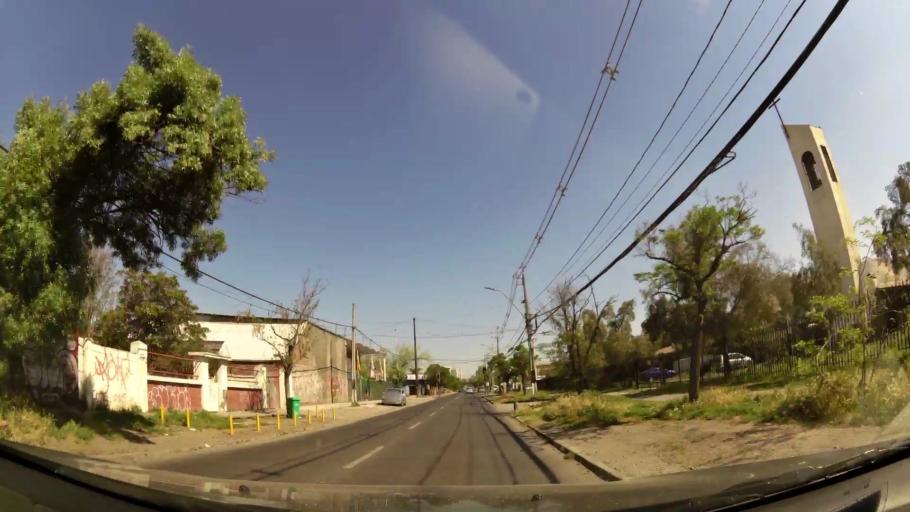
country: CL
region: Santiago Metropolitan
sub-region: Provincia de Maipo
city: San Bernardo
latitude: -33.5843
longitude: -70.7060
